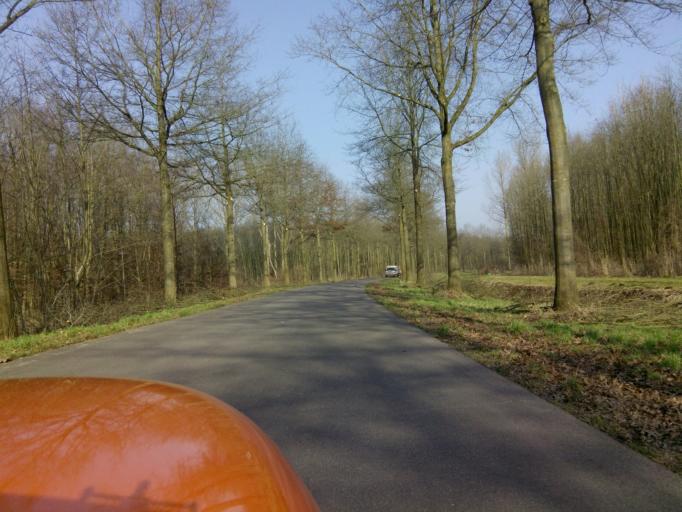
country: NL
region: Utrecht
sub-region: Gemeente Bunschoten
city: Bunschoten
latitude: 52.2652
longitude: 5.4368
